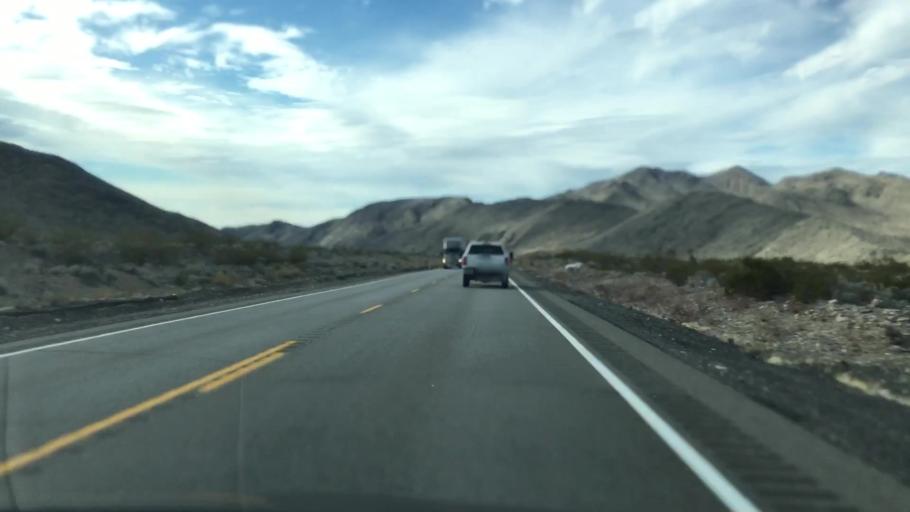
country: US
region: Nevada
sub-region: Nye County
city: Pahrump
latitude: 36.5890
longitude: -116.0468
